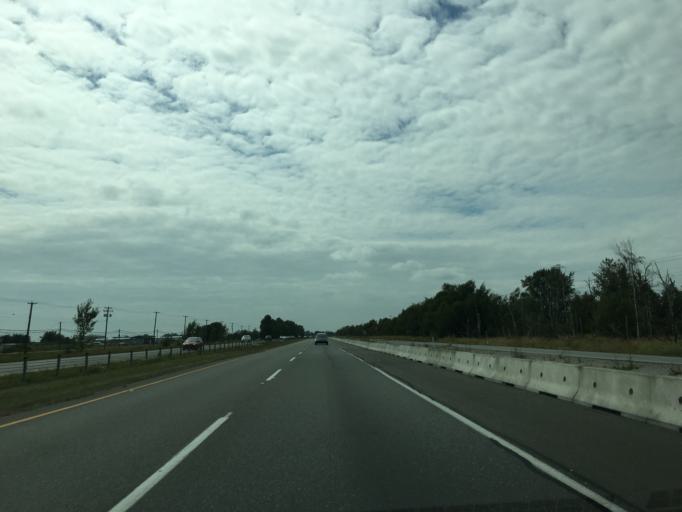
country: CA
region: British Columbia
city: Delta
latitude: 49.0905
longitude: -122.9823
